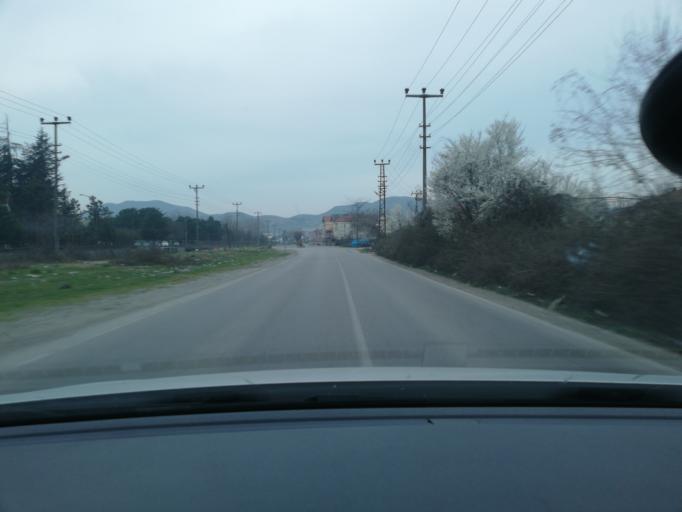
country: TR
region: Zonguldak
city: Caycuma
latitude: 41.4144
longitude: 32.1012
